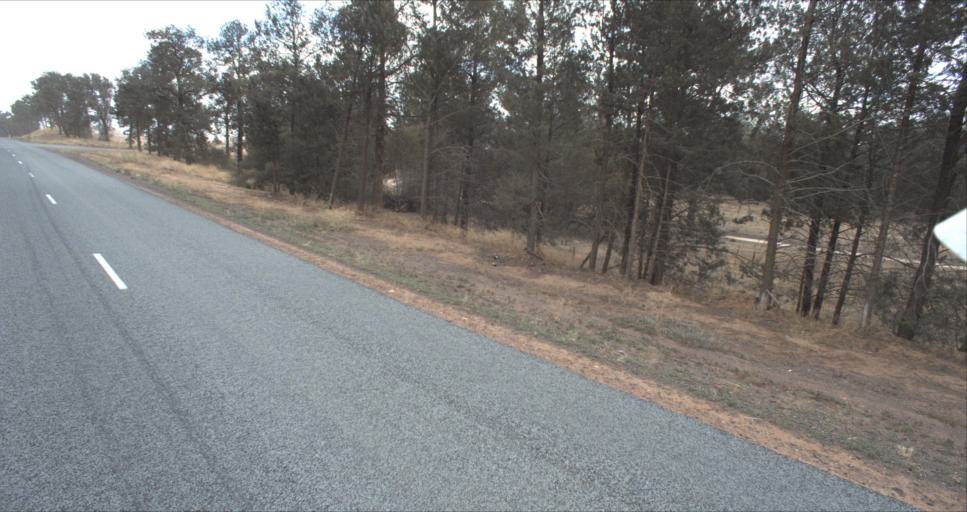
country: AU
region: New South Wales
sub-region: Leeton
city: Leeton
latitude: -34.6572
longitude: 146.3500
